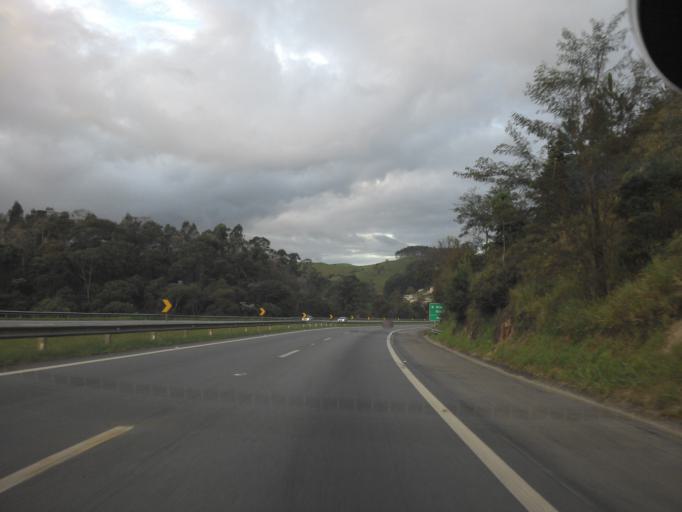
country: BR
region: Sao Paulo
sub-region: Santa Isabel
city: Santa Isabel
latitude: -23.1645
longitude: -46.2278
